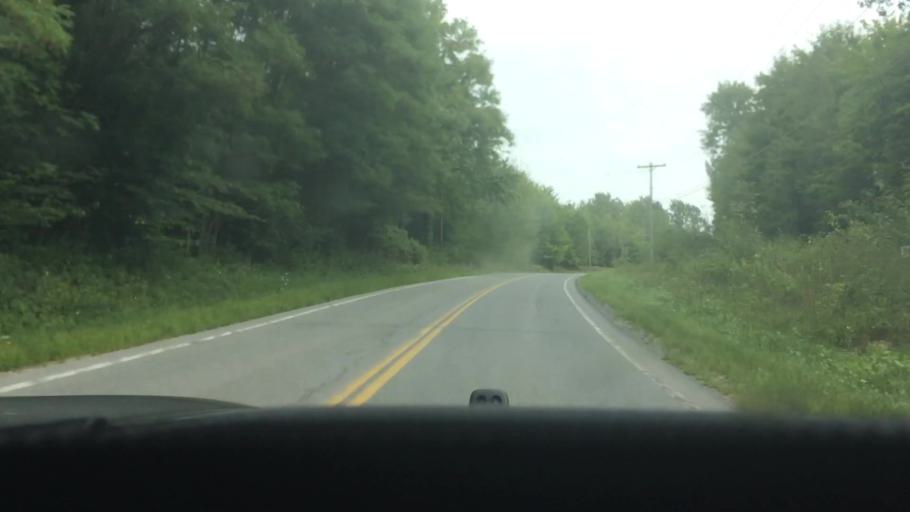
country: US
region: New York
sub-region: St. Lawrence County
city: Canton
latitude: 44.5140
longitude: -75.2038
